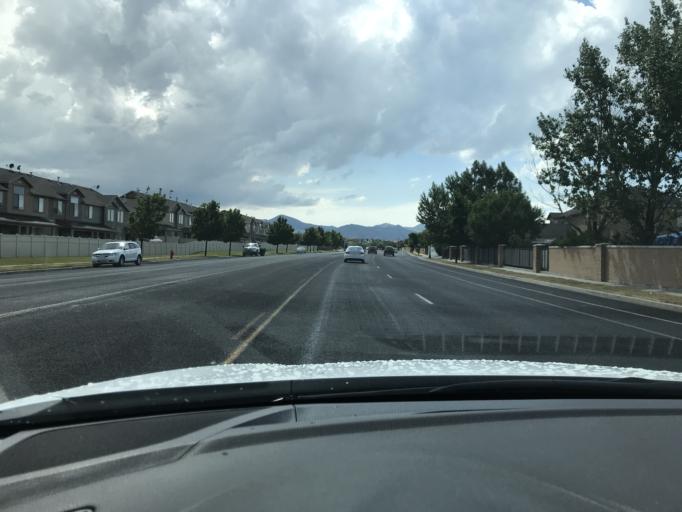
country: US
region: Utah
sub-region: Salt Lake County
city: South Jordan Heights
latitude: 40.5619
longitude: -111.9824
